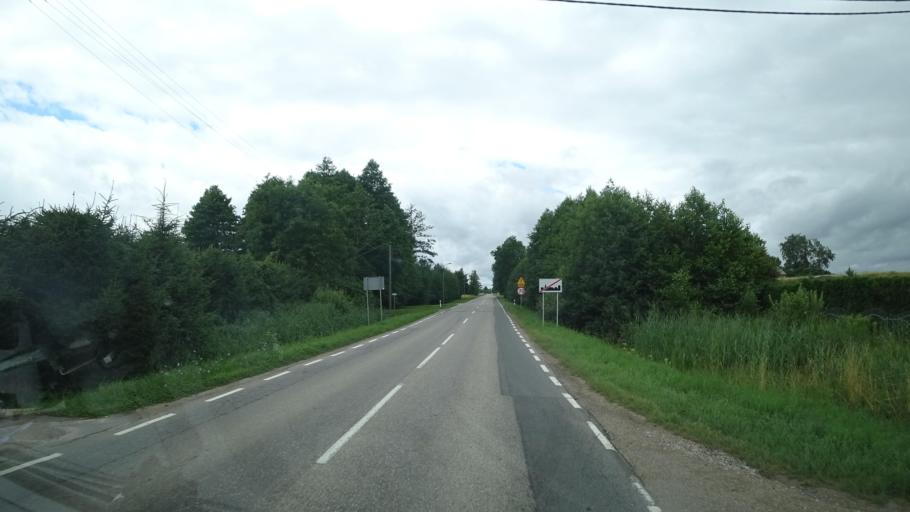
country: PL
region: Warmian-Masurian Voivodeship
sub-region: Powiat olecki
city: Olecko
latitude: 54.0721
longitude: 22.4761
